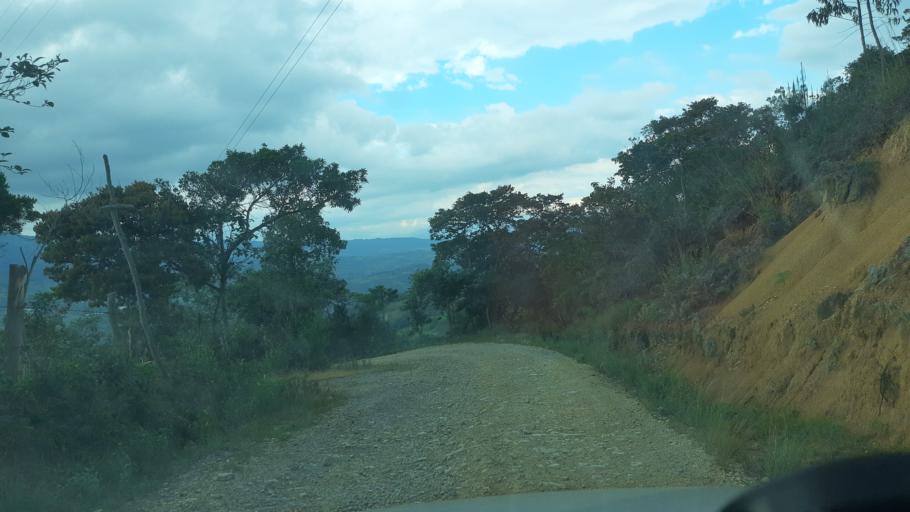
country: CO
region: Boyaca
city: Santa Sofia
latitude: 5.7451
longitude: -73.5629
